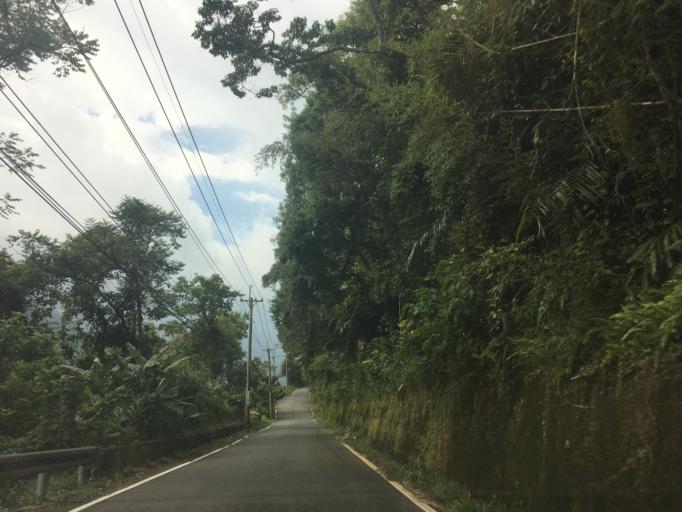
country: TW
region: Taiwan
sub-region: Miaoli
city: Miaoli
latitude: 24.3637
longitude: 120.9602
